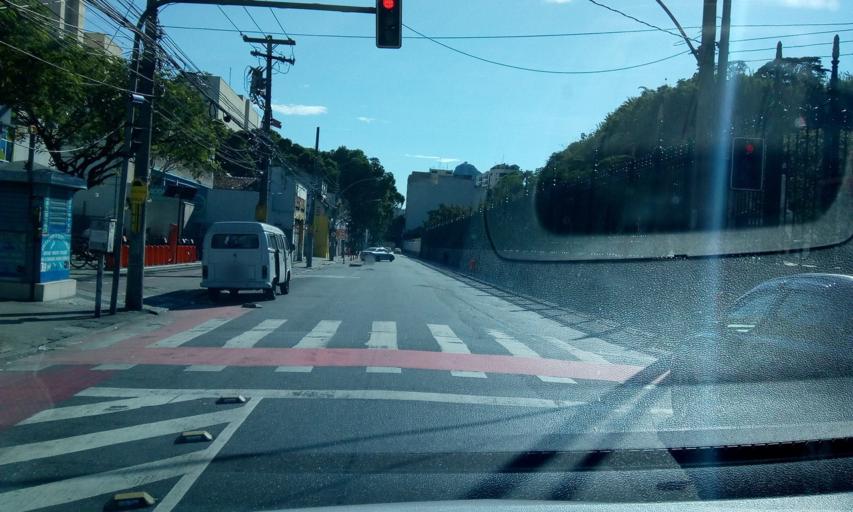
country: BR
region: Rio de Janeiro
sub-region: Rio De Janeiro
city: Rio de Janeiro
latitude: -22.9573
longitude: -43.1892
